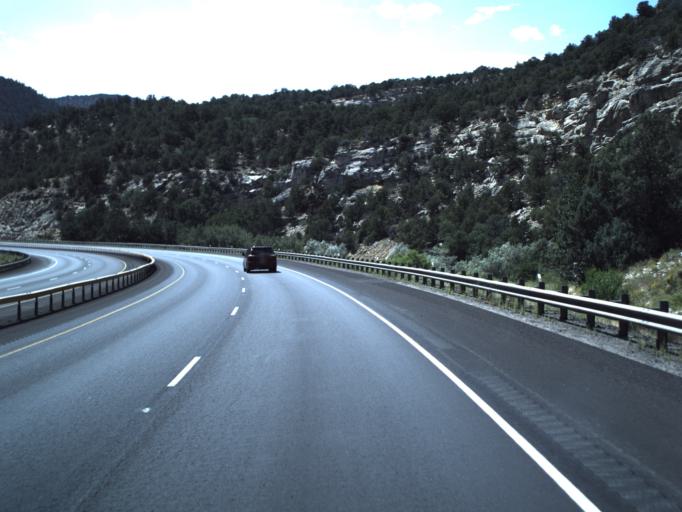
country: US
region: Utah
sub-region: Sevier County
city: Salina
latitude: 38.9053
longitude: -111.6407
